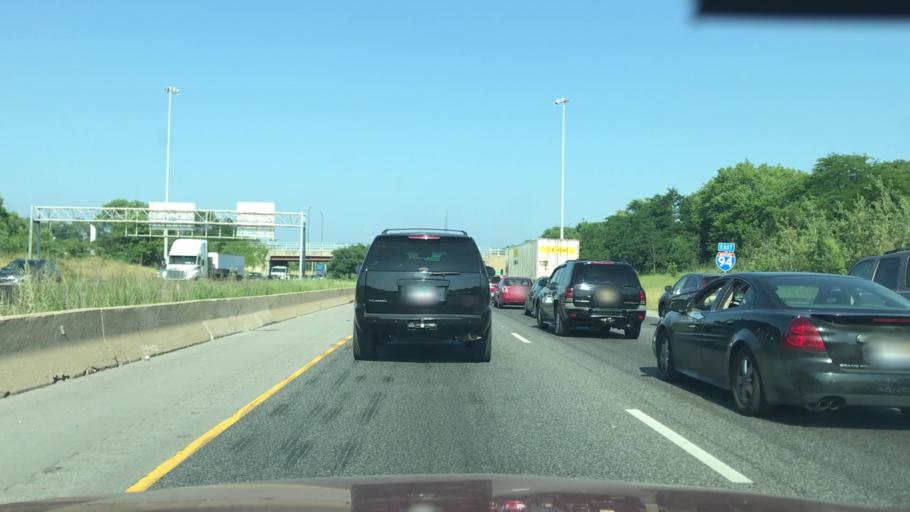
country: US
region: Illinois
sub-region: Cook County
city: Calumet Park
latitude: 41.7132
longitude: -87.6166
